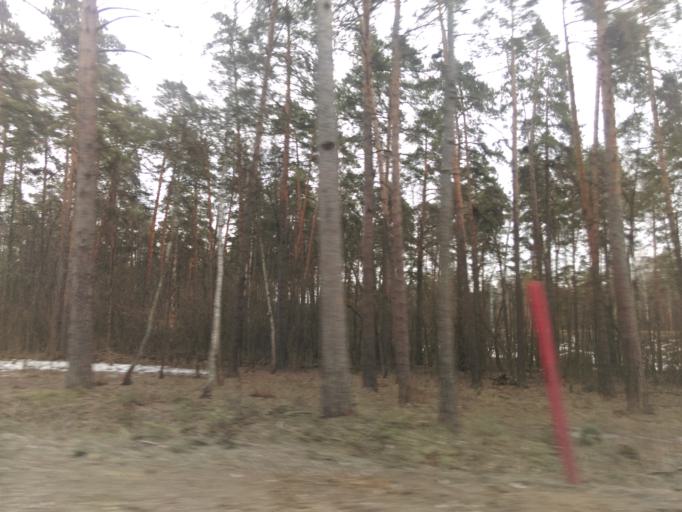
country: RU
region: Moskovskaya
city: Nemchinovka
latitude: 55.7509
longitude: 37.3315
